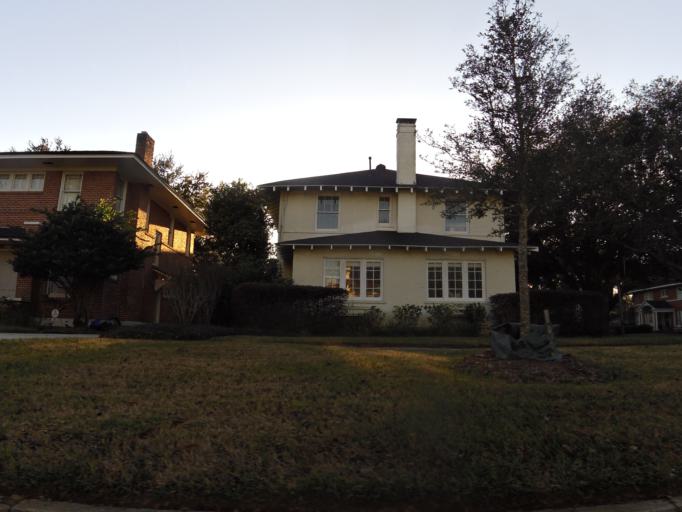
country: US
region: Florida
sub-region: Duval County
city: Jacksonville
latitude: 30.3011
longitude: -81.7014
